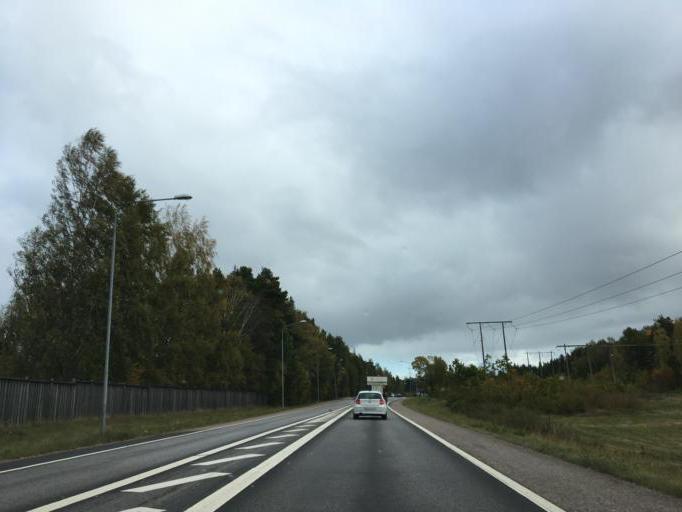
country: SE
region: Soedermanland
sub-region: Nykopings Kommun
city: Nykoping
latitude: 58.7657
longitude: 16.9788
